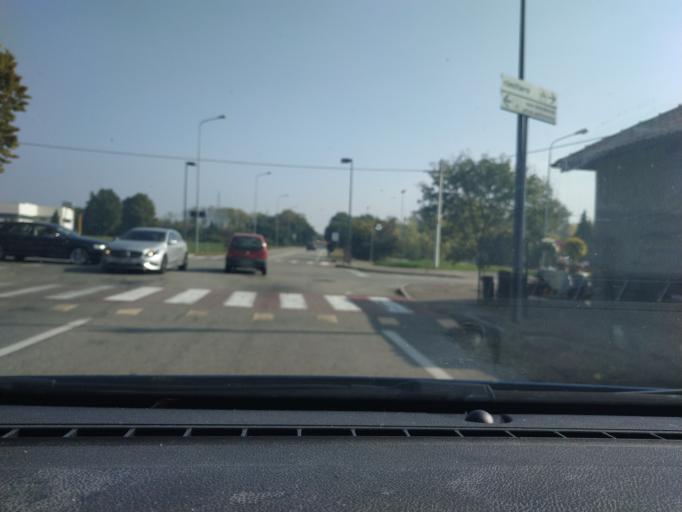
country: IT
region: Piedmont
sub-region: Provincia di Biella
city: Occhieppo Inferiore
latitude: 45.5510
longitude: 8.0373
